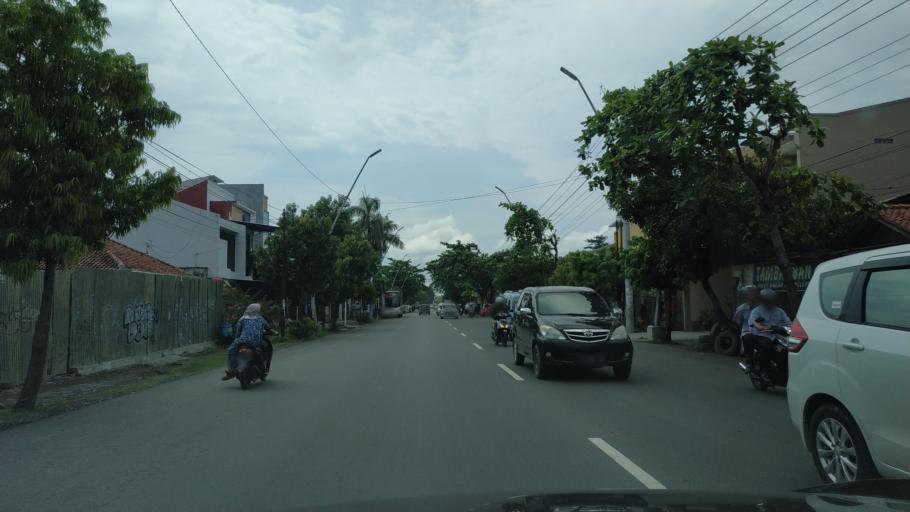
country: ID
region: Central Java
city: Tegal
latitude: -6.8814
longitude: 109.1265
